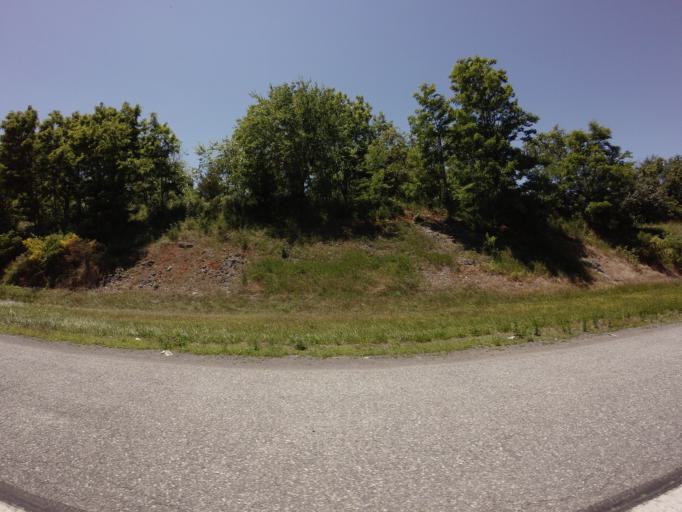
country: US
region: West Virginia
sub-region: Jefferson County
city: Ranson
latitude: 39.3133
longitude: -77.8456
